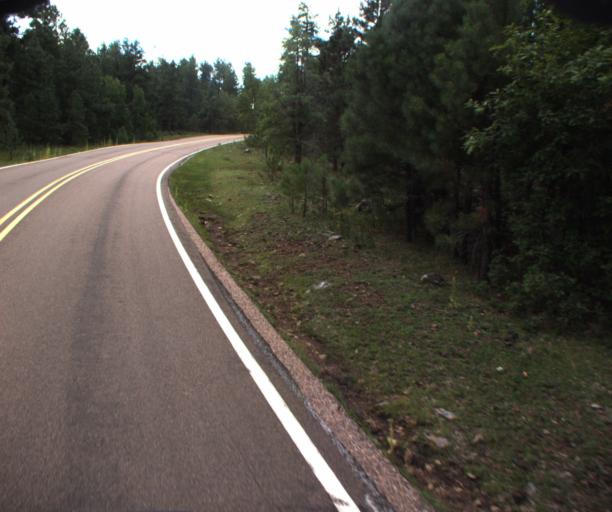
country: US
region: Arizona
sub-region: Navajo County
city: Pinetop-Lakeside
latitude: 34.0193
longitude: -109.7818
